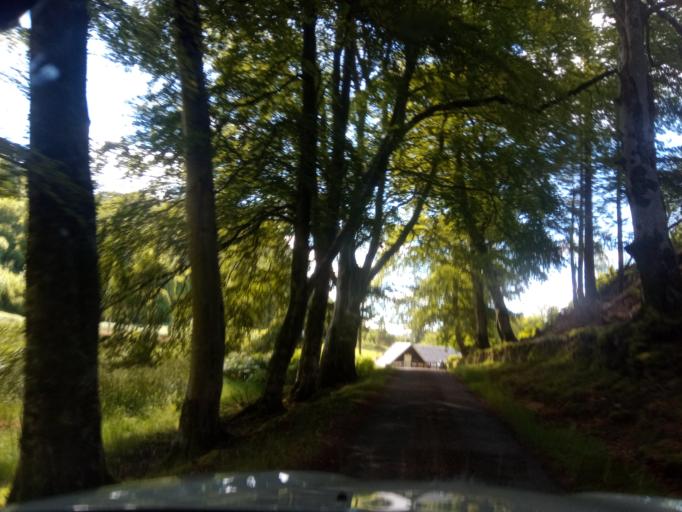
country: GB
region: Scotland
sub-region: Argyll and Bute
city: Isle Of Mull
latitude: 56.7775
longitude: -5.8245
